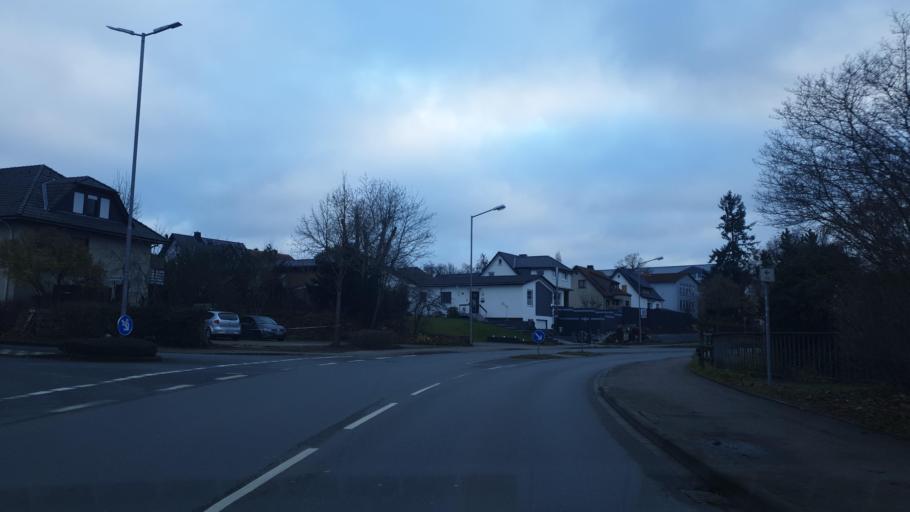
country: DE
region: North Rhine-Westphalia
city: Loehne
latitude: 52.1874
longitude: 8.6890
